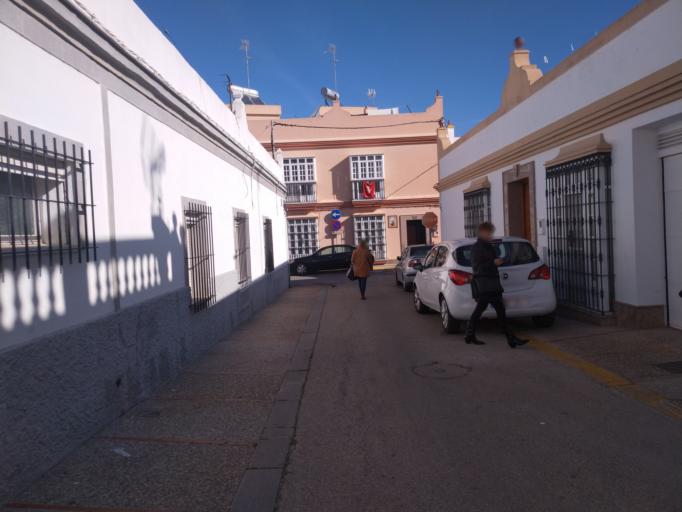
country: ES
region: Andalusia
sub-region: Provincia de Cadiz
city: San Fernando
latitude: 36.4733
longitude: -6.1964
